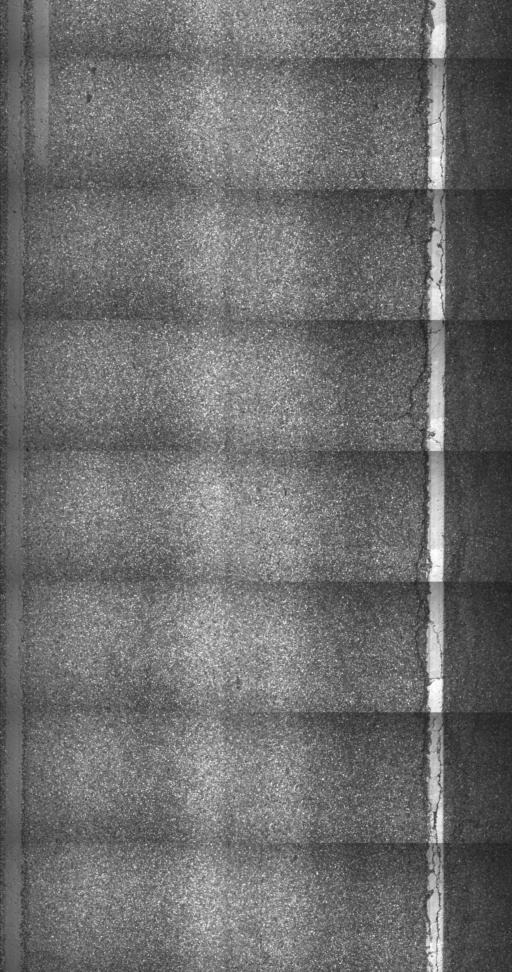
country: US
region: Vermont
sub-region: Bennington County
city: Manchester Center
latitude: 43.2036
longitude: -73.0596
